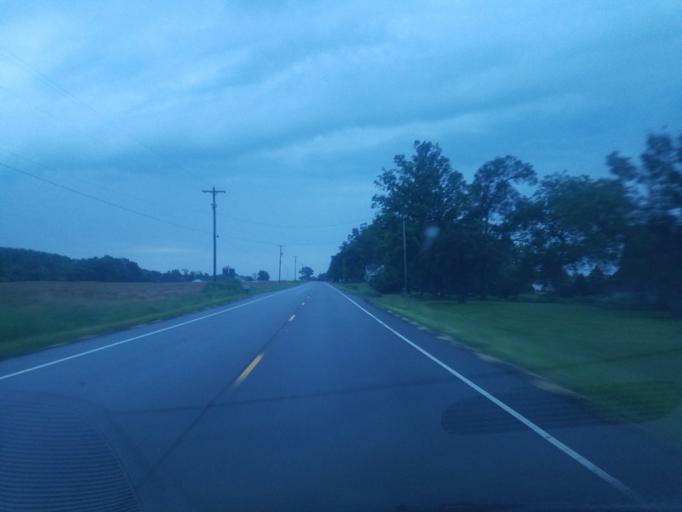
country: US
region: Ohio
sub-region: Mahoning County
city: Canfield
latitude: 40.9868
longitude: -80.7588
